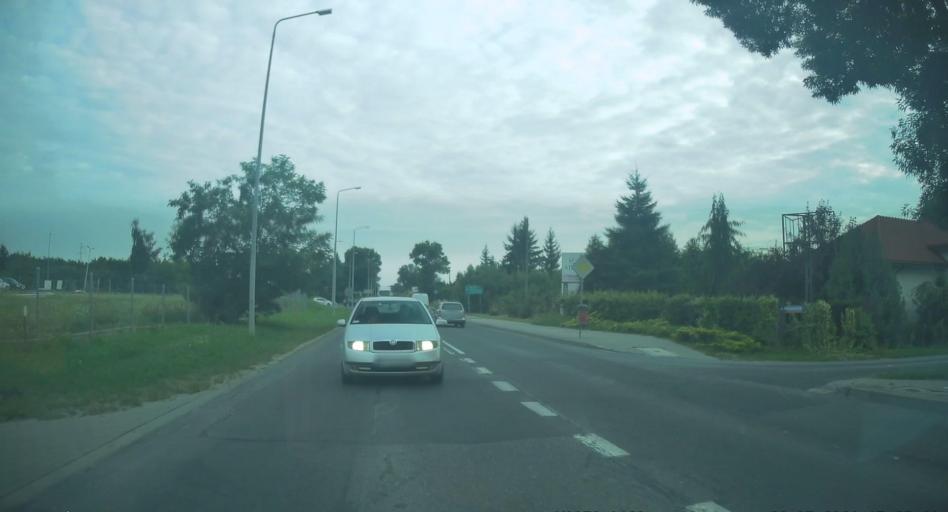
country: PL
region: Lodz Voivodeship
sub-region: Powiat radomszczanski
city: Radomsko
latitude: 51.0546
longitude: 19.4403
